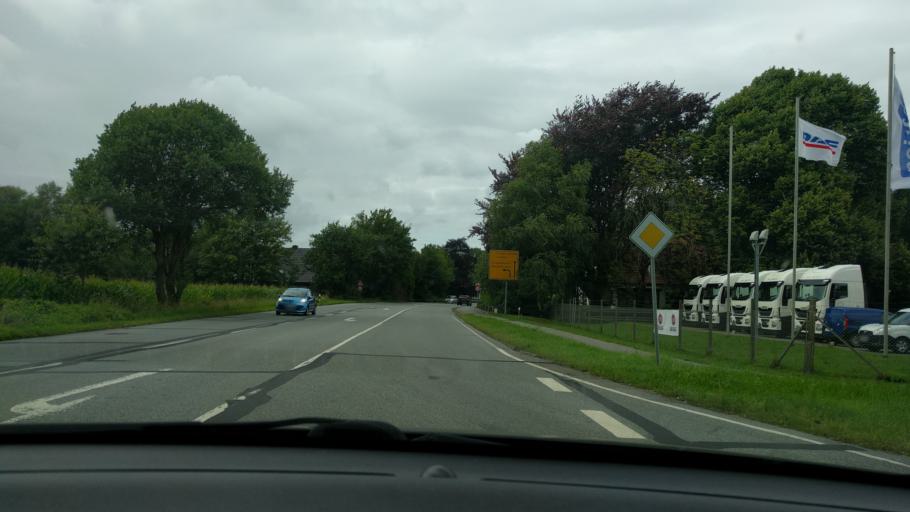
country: DE
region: Schleswig-Holstein
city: Weddingstedt
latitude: 54.2299
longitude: 9.0798
